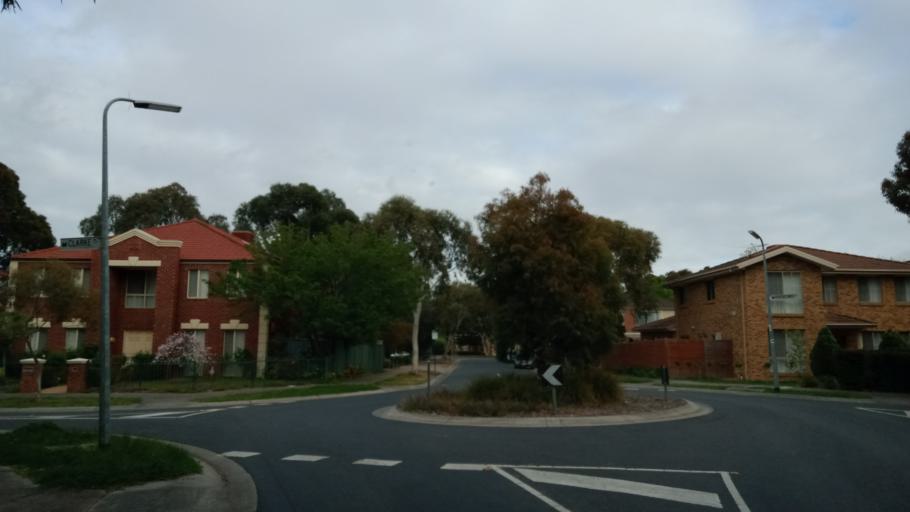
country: AU
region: Victoria
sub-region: Monash
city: Notting Hill
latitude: -37.8772
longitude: 145.1404
